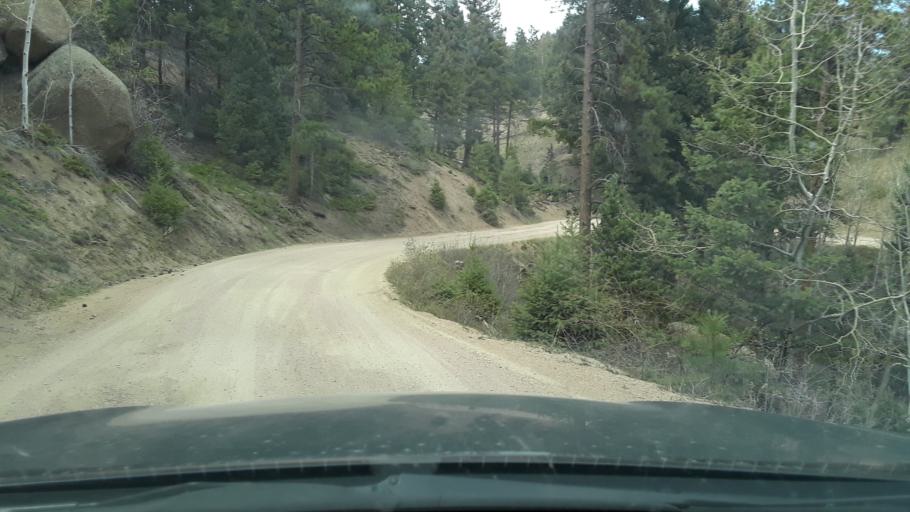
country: US
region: Colorado
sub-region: El Paso County
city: Palmer Lake
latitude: 39.0709
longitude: -104.9364
